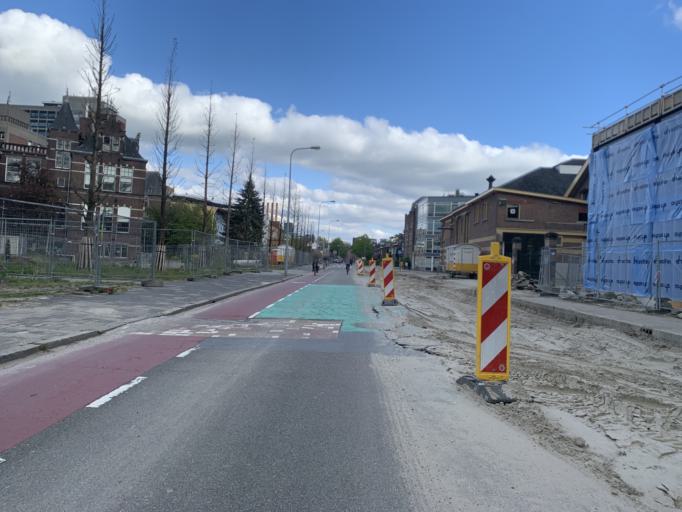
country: NL
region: Groningen
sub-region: Gemeente Groningen
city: Groningen
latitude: 53.2242
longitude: 6.5686
